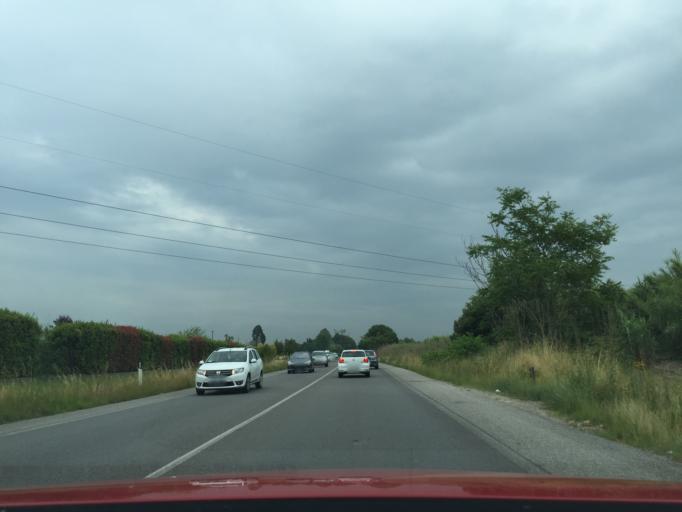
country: IT
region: Tuscany
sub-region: Provincia di Pistoia
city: Stazione Masotti
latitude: 43.9125
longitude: 10.8738
